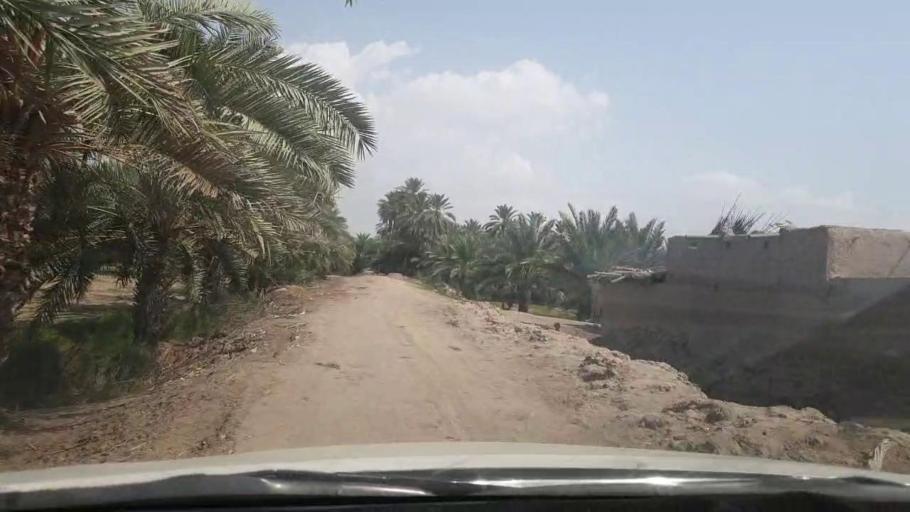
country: PK
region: Sindh
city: Khairpur
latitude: 27.5534
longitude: 68.8444
